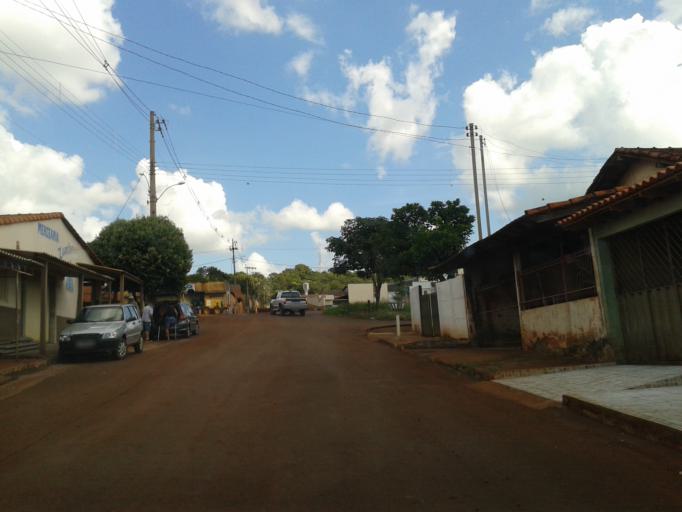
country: BR
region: Minas Gerais
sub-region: Capinopolis
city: Capinopolis
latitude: -18.6863
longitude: -49.5804
